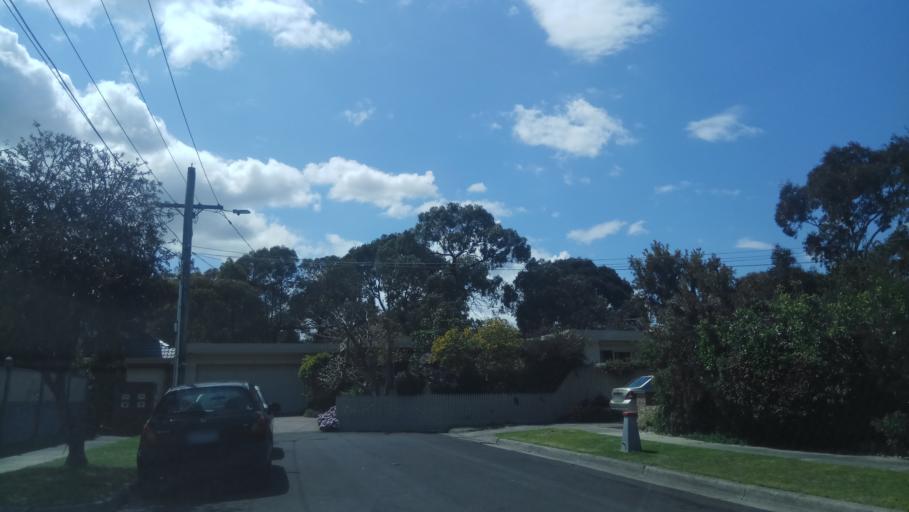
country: AU
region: Victoria
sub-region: Kingston
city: Dingley Village
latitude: -37.9812
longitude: 145.1318
